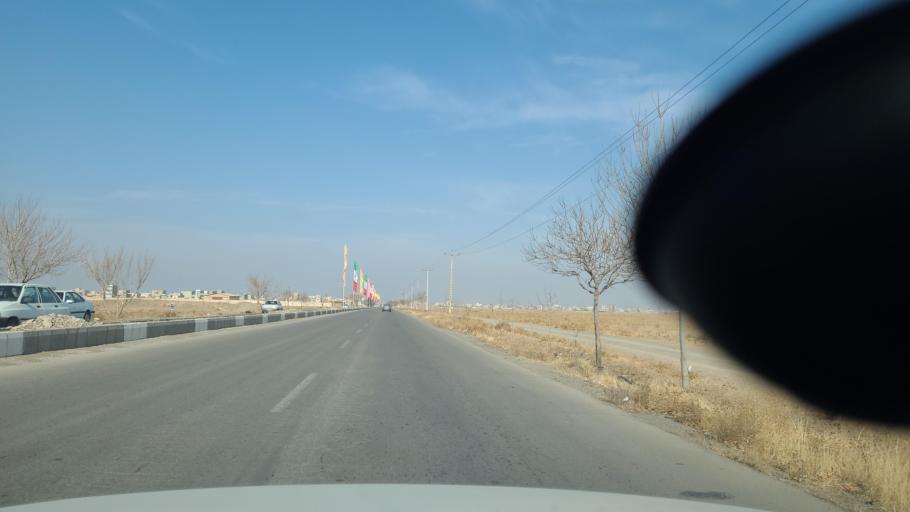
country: IR
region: Razavi Khorasan
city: Fariman
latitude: 35.6755
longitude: 59.8426
